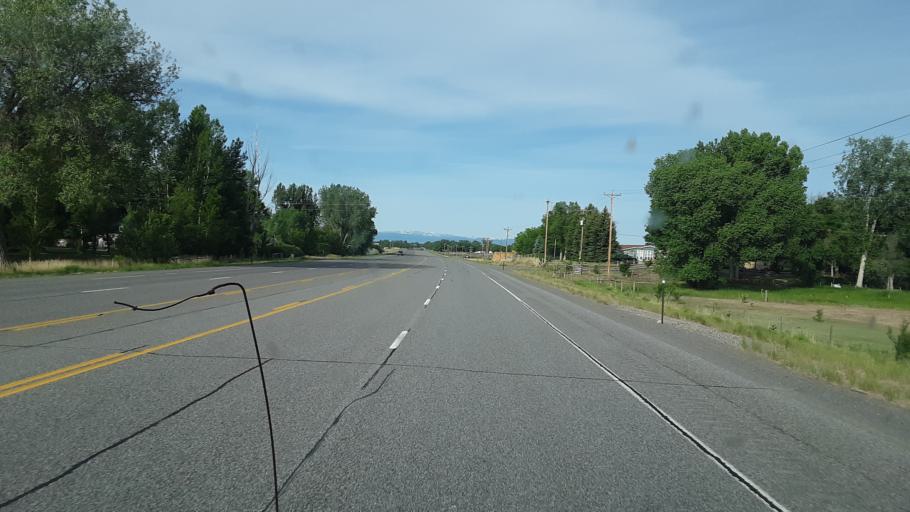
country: US
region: Wyoming
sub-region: Fremont County
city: Riverton
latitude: 43.1050
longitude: -108.3482
